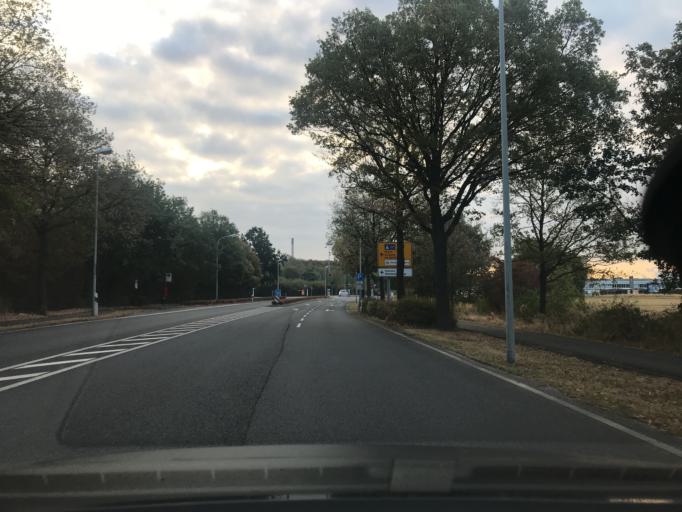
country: DE
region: North Rhine-Westphalia
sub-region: Regierungsbezirk Dusseldorf
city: Krefeld
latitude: 51.3761
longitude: 6.6325
